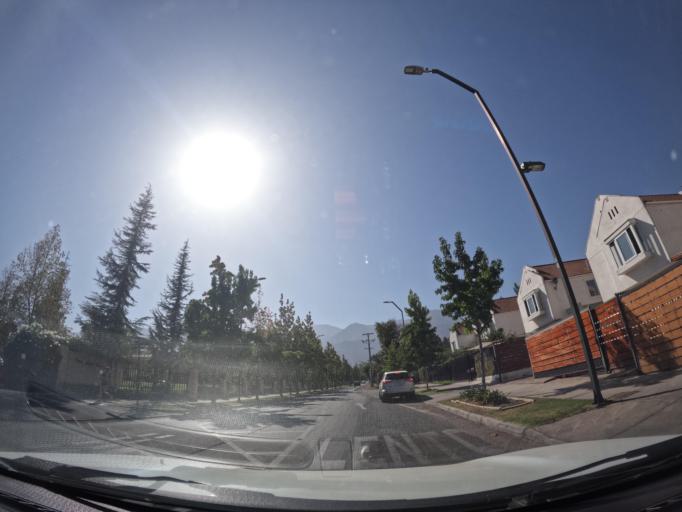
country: CL
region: Santiago Metropolitan
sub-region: Provincia de Santiago
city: Villa Presidente Frei, Nunoa, Santiago, Chile
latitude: -33.5079
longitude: -70.5513
